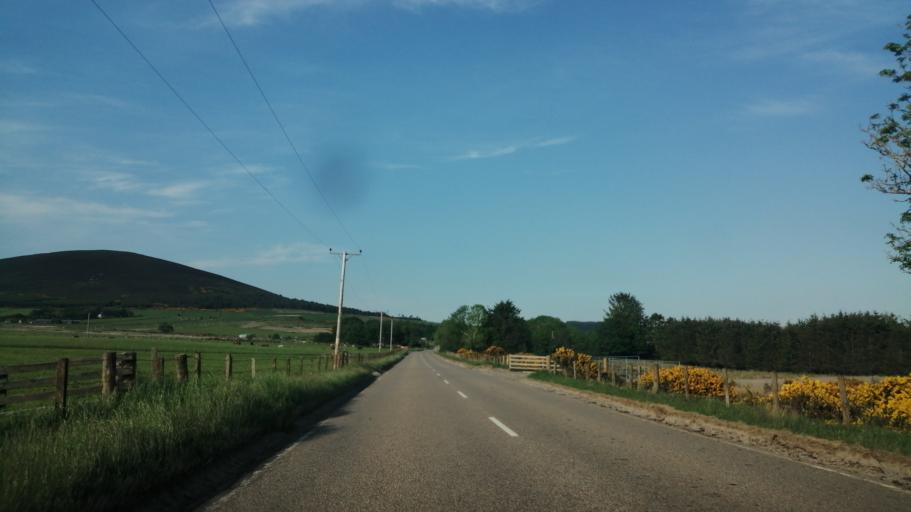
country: GB
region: Scotland
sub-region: Aberdeenshire
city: Huntly
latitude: 57.5632
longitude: -2.7963
